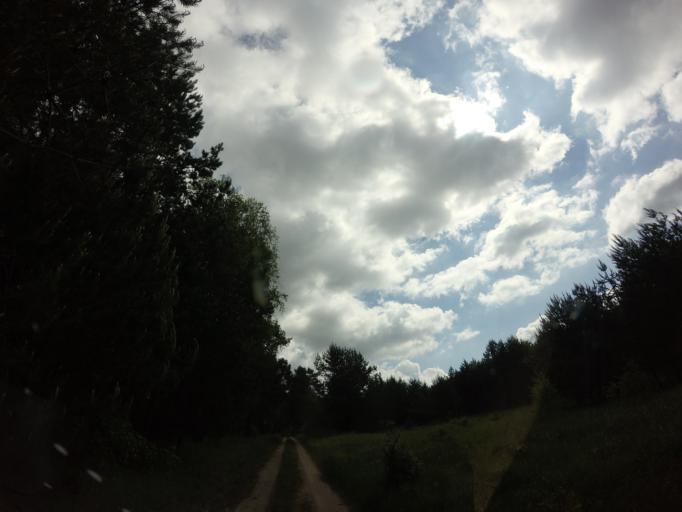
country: PL
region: West Pomeranian Voivodeship
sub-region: Powiat choszczenski
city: Drawno
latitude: 53.1790
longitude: 15.6949
